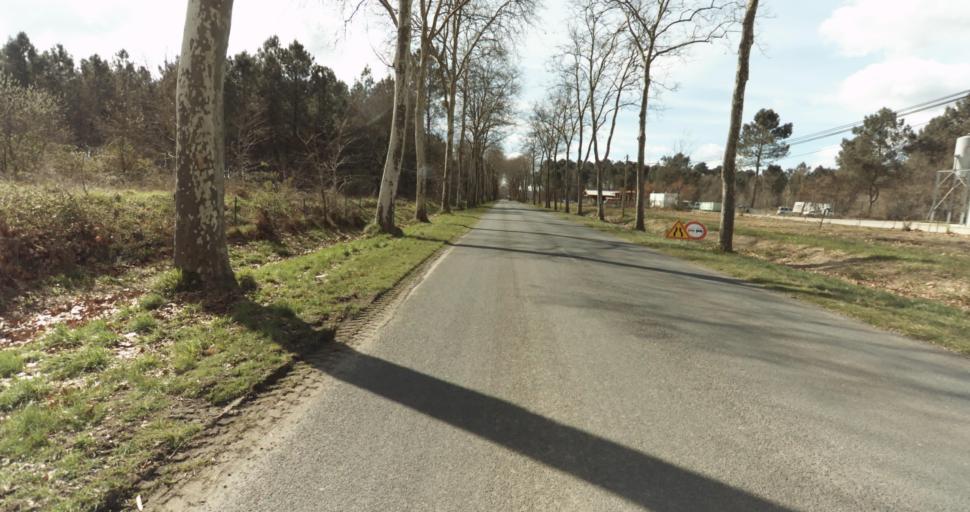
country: FR
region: Aquitaine
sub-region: Departement des Landes
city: Roquefort
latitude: 44.0518
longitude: -0.3196
